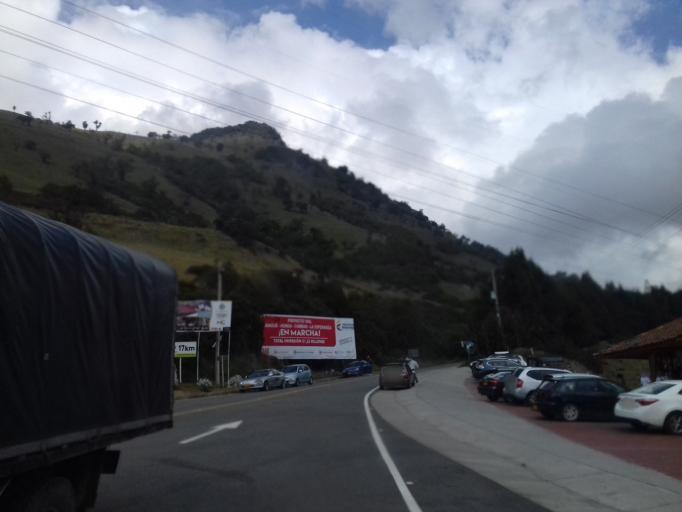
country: CO
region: Caldas
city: Villamaria
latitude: 5.0146
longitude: -75.3408
